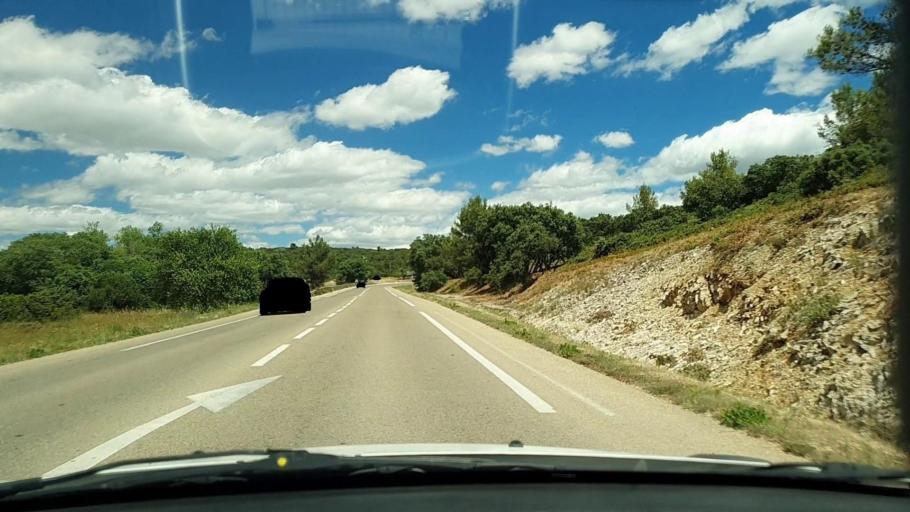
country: FR
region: Languedoc-Roussillon
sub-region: Departement du Gard
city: Poulx
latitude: 43.8893
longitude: 4.4169
